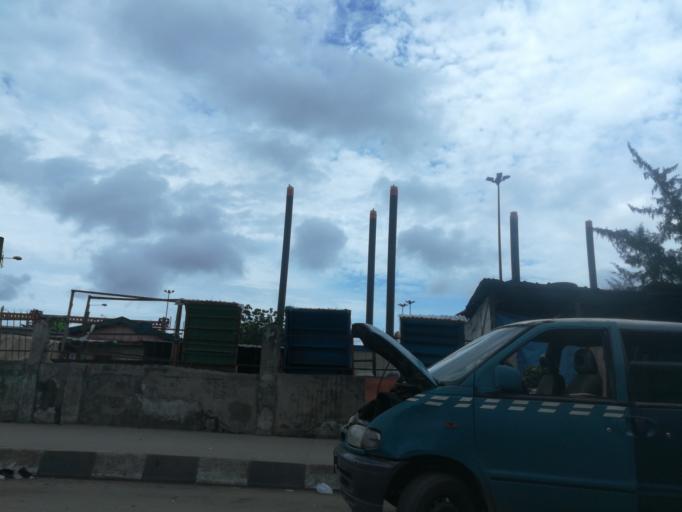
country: NG
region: Lagos
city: Lagos
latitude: 6.4540
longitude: 3.3849
